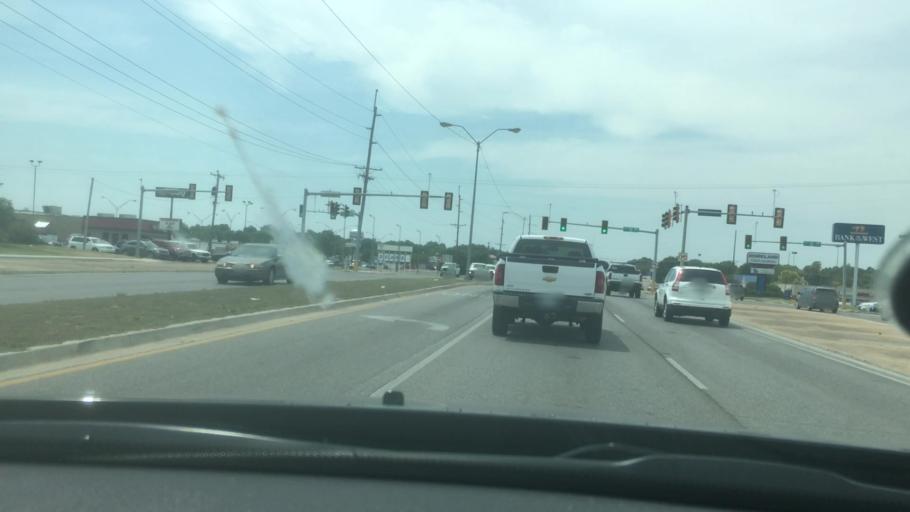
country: US
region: Oklahoma
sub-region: Carter County
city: Ardmore
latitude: 34.1810
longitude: -97.1431
